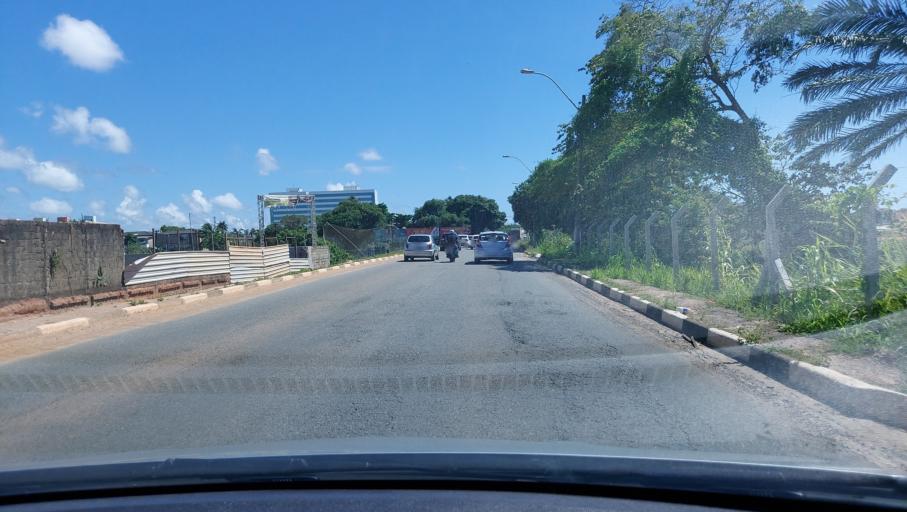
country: BR
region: Bahia
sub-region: Lauro De Freitas
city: Lauro de Freitas
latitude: -12.9006
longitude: -38.3307
